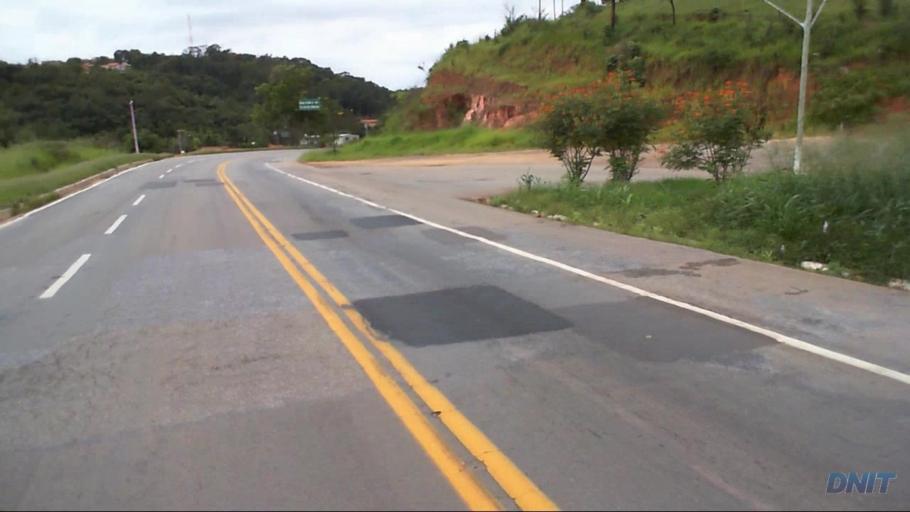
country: BR
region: Minas Gerais
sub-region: Barao De Cocais
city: Barao de Cocais
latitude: -19.8316
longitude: -43.3583
